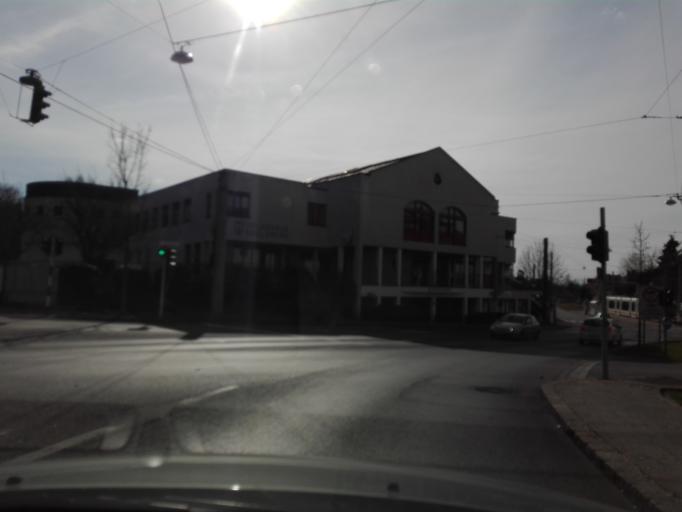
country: AT
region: Upper Austria
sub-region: Politischer Bezirk Linz-Land
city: Ansfelden
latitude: 48.2444
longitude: 14.3292
